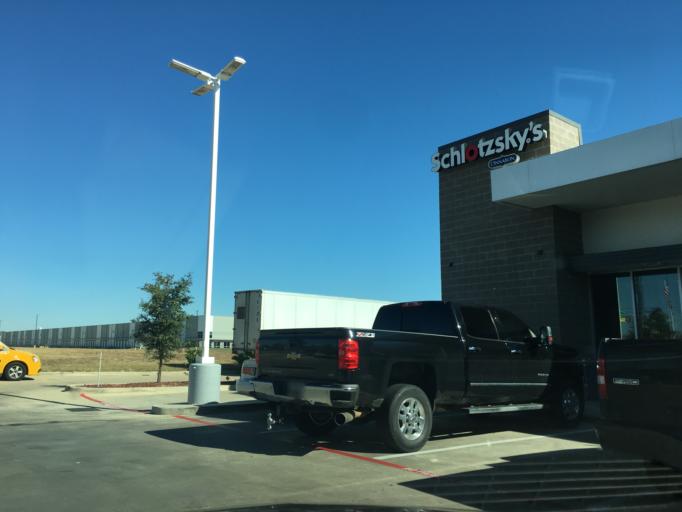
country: US
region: Texas
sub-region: Harris County
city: Humble
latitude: 29.9828
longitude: -95.2755
